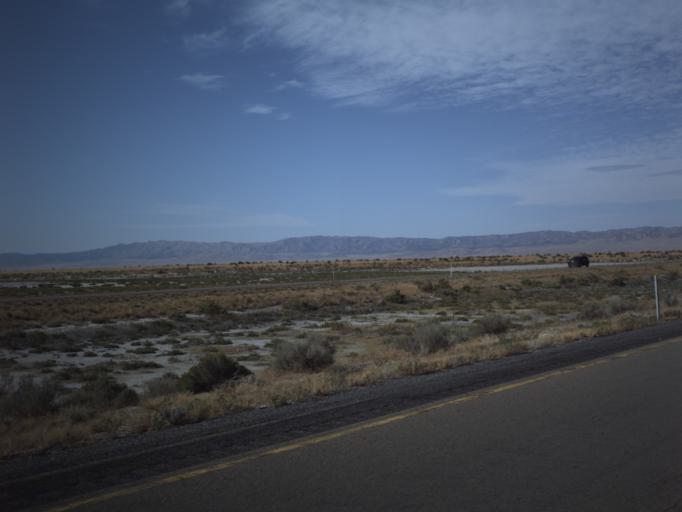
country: US
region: Utah
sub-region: Tooele County
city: Grantsville
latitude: 40.7469
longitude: -112.6605
